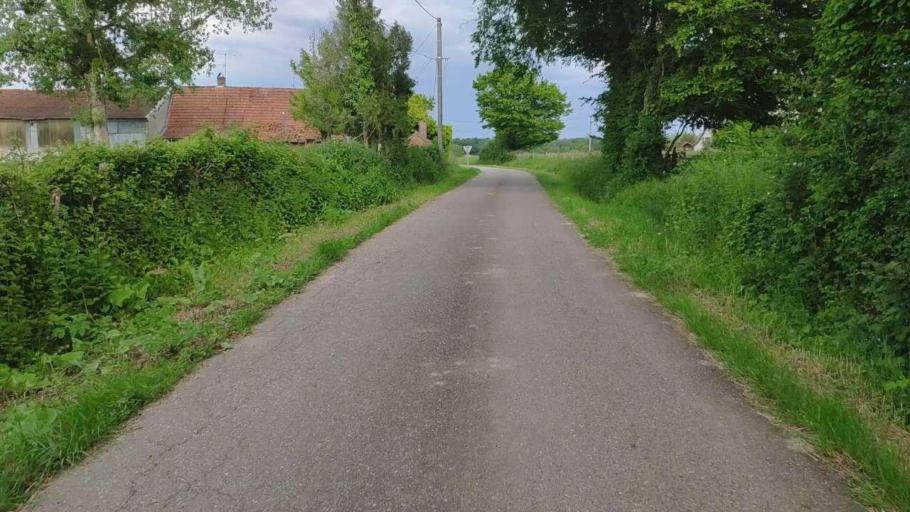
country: FR
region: Bourgogne
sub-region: Departement de Saone-et-Loire
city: Saint-Germain-du-Bois
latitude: 46.7989
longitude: 5.3406
